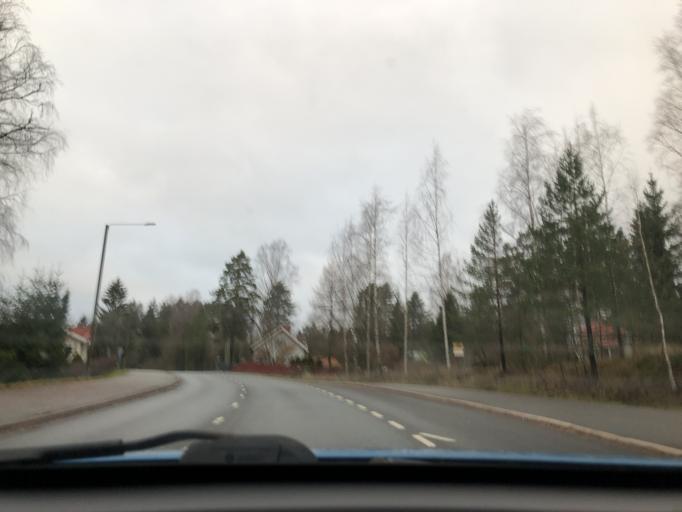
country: FI
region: Pirkanmaa
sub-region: Tampere
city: Kangasala
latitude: 61.5290
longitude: 24.0103
